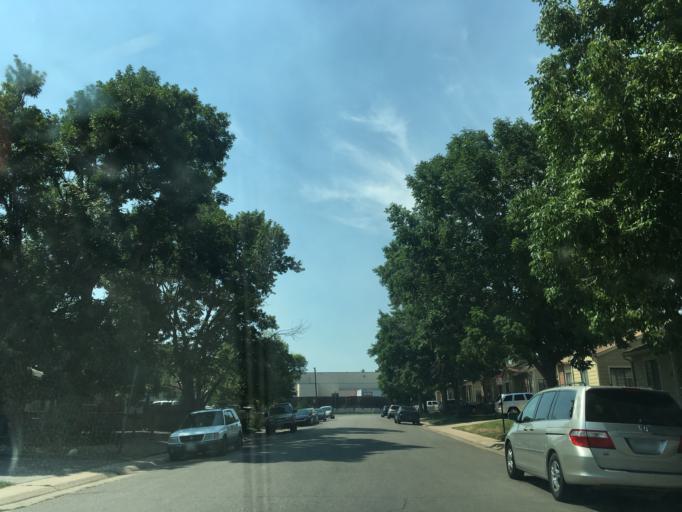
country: US
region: Colorado
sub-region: Jefferson County
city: Lakewood
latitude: 39.6925
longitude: -105.0519
